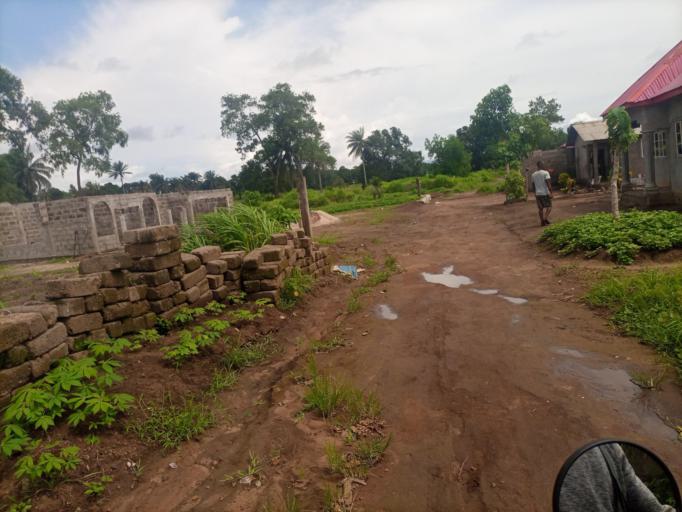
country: SL
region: Northern Province
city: Sawkta
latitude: 8.6363
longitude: -13.2081
